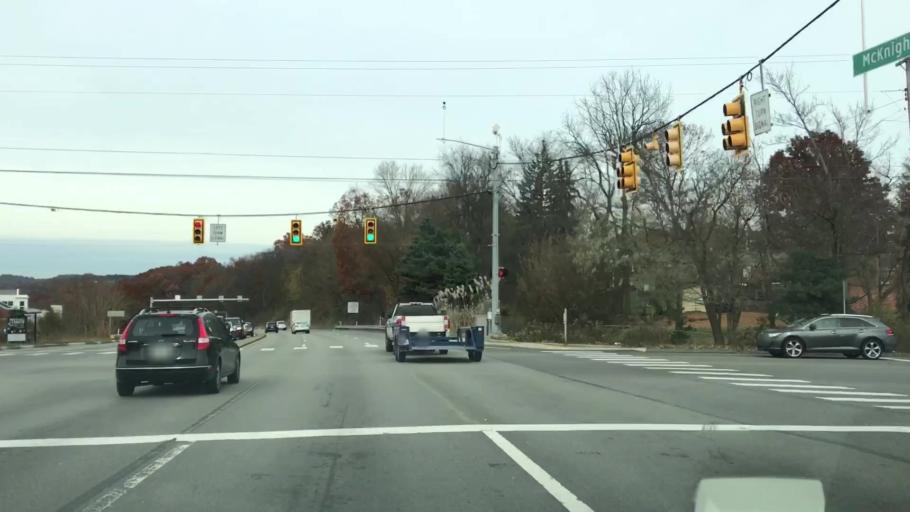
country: US
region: Pennsylvania
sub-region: Allegheny County
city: West View
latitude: 40.5720
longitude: -80.0235
